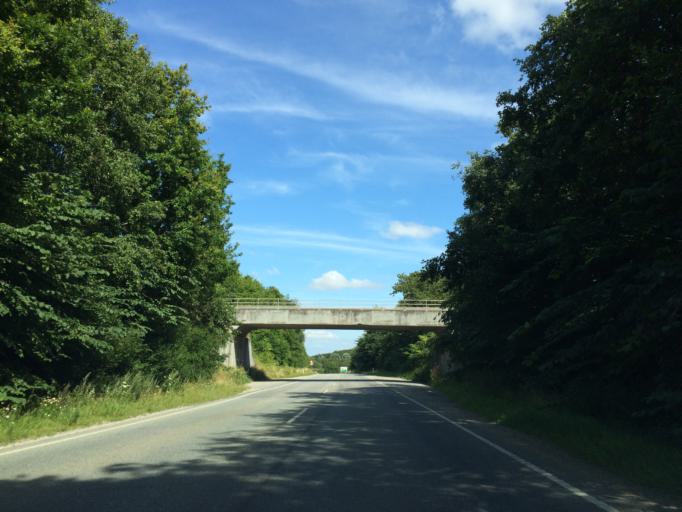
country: DK
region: Central Jutland
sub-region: Arhus Kommune
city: Logten
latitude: 56.2886
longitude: 10.3250
